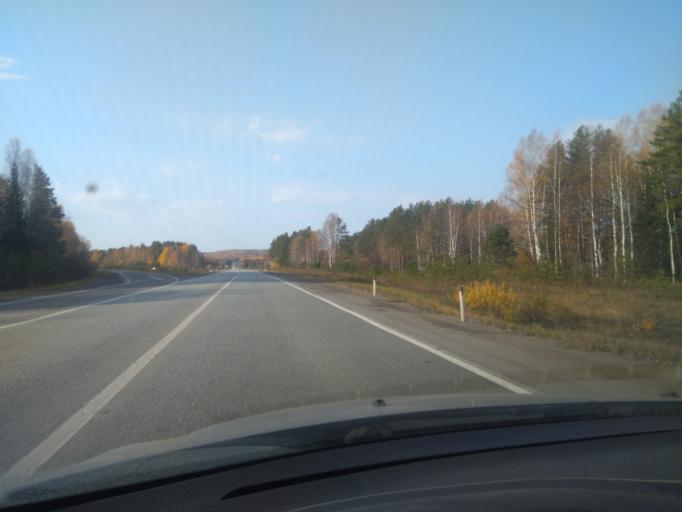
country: RU
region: Sverdlovsk
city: Atig
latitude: 56.7352
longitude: 59.4366
